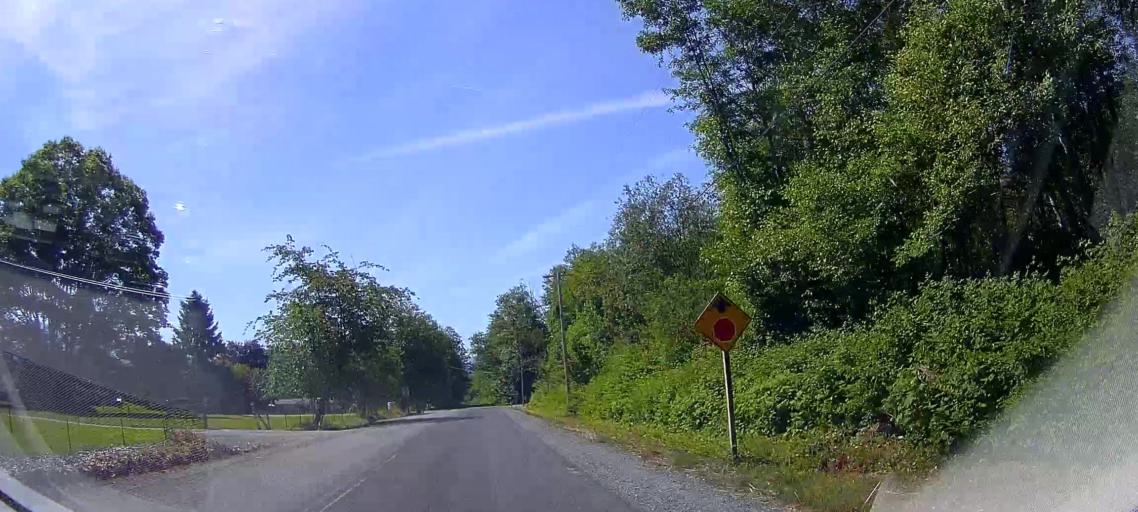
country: US
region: Washington
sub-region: Skagit County
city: Sedro-Woolley
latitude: 48.5294
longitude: -122.2481
